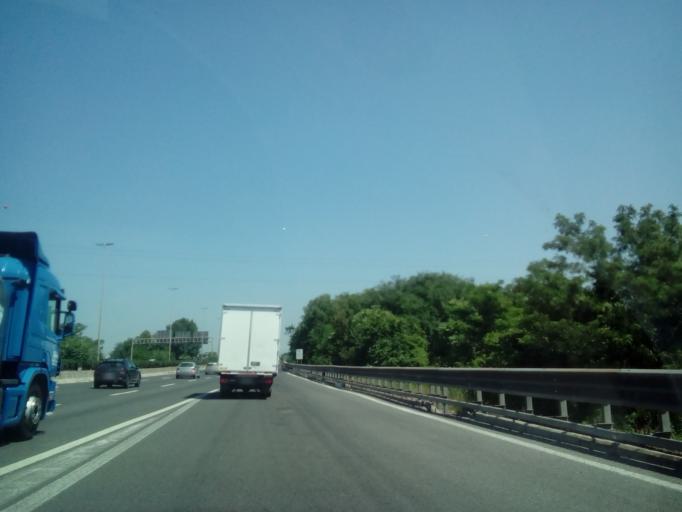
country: IT
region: Latium
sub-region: Citta metropolitana di Roma Capitale
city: Setteville
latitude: 41.8968
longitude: 12.6155
